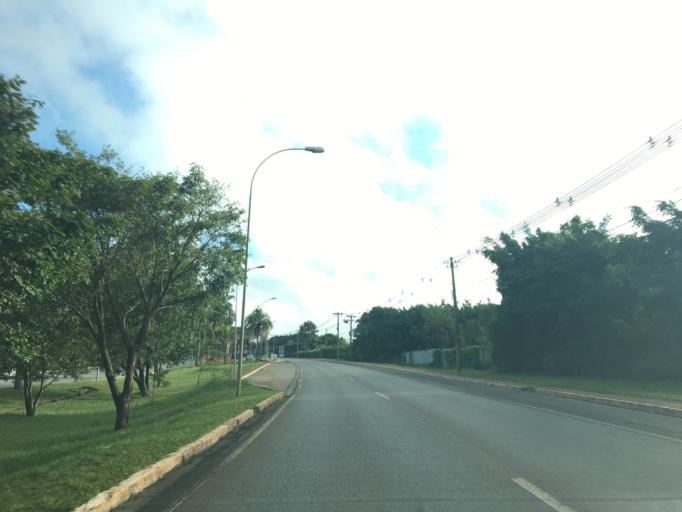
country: BR
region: Federal District
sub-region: Brasilia
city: Brasilia
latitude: -15.8222
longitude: -47.8050
